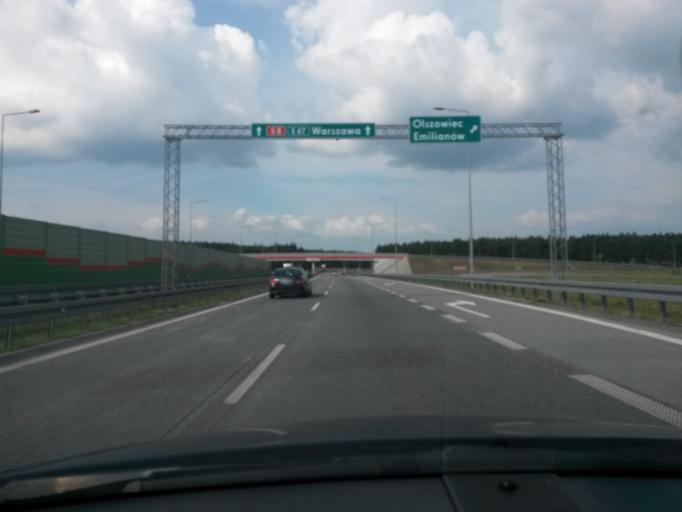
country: PL
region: Lodz Voivodeship
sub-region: Powiat tomaszowski
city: Lubochnia
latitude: 51.6222
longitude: 20.0944
